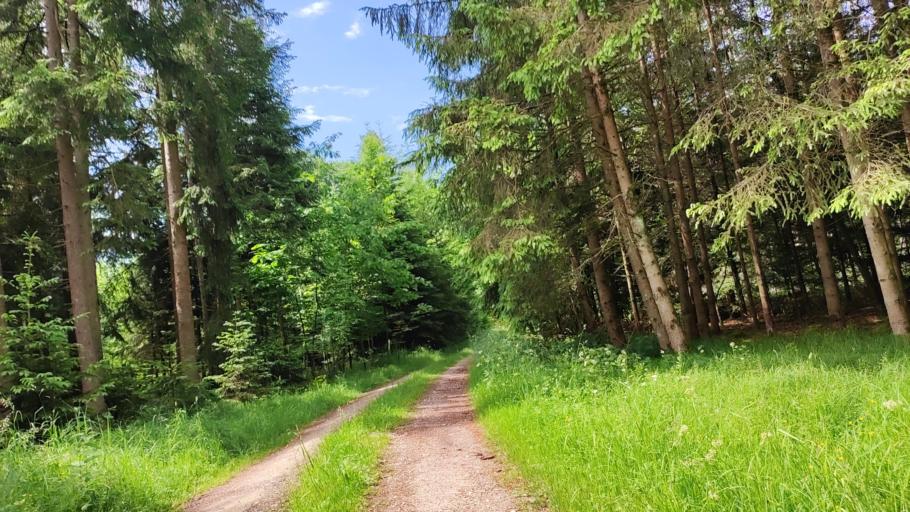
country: DE
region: Bavaria
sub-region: Swabia
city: Landensberg
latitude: 48.4312
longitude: 10.5420
